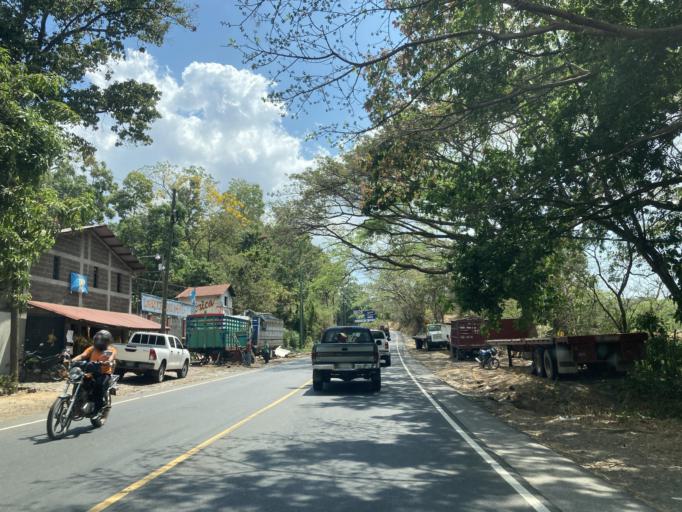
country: GT
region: Santa Rosa
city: Guazacapan
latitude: 14.0697
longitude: -90.4166
